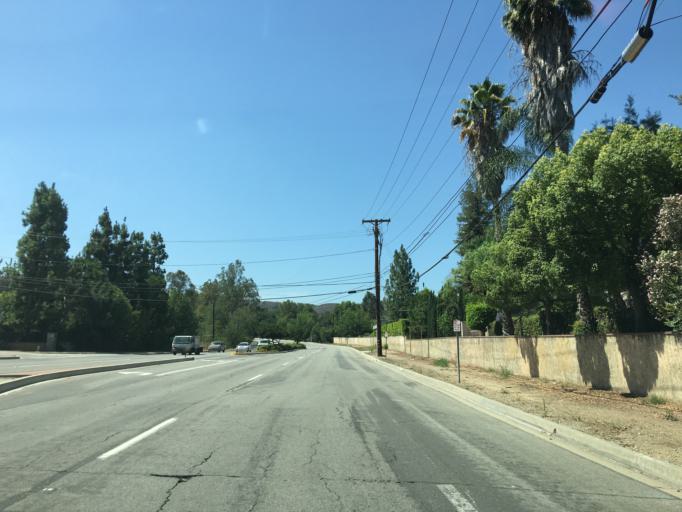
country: US
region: California
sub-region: Los Angeles County
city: Covina
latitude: 34.0620
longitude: -117.8685
